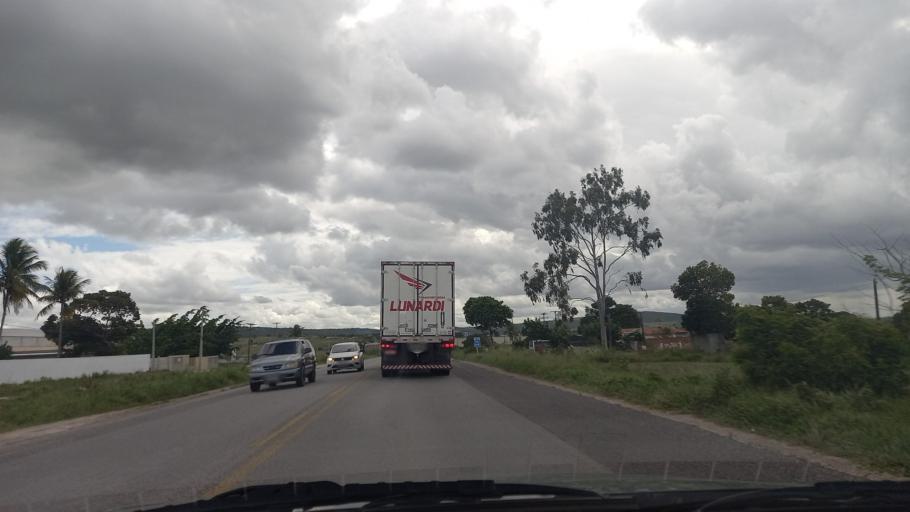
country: BR
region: Pernambuco
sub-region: Lajedo
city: Lajedo
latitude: -8.6637
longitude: -36.3536
